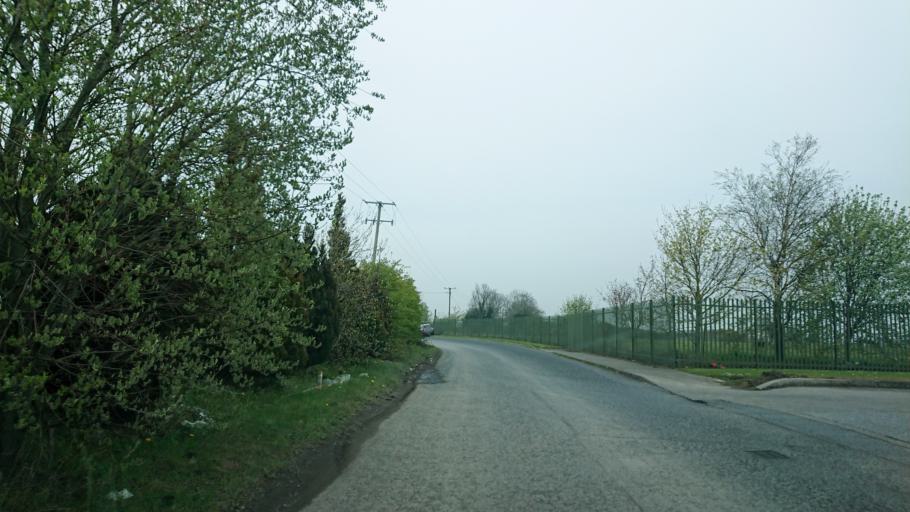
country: IE
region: Leinster
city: Ballymun
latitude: 53.4118
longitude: -6.2611
